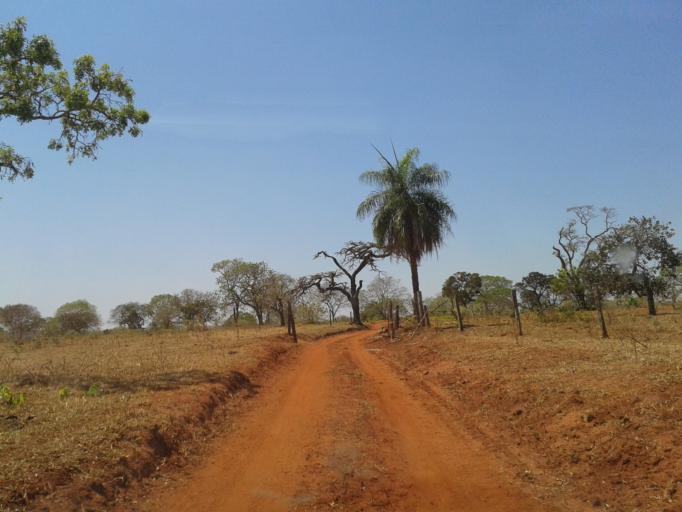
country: BR
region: Minas Gerais
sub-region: Ituiutaba
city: Ituiutaba
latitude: -19.0682
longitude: -49.3674
